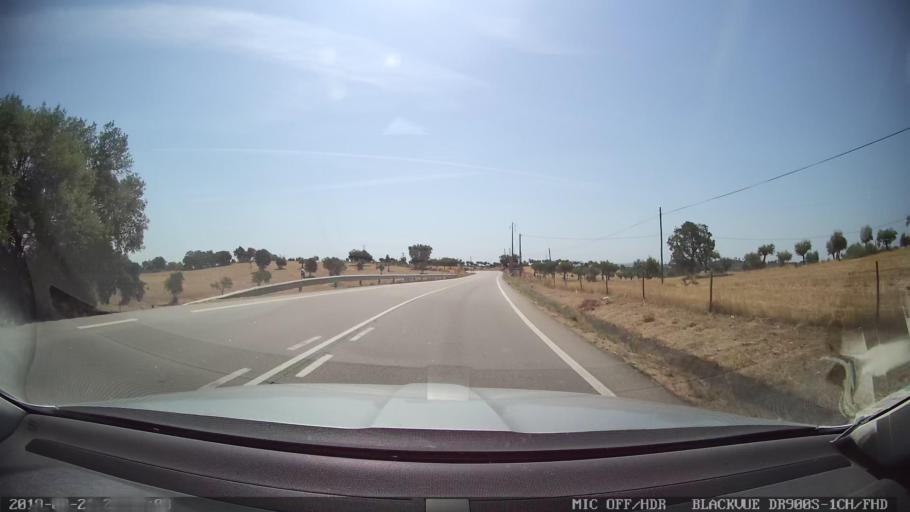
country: PT
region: Guarda
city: Alcains
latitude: 39.8708
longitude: -7.3651
